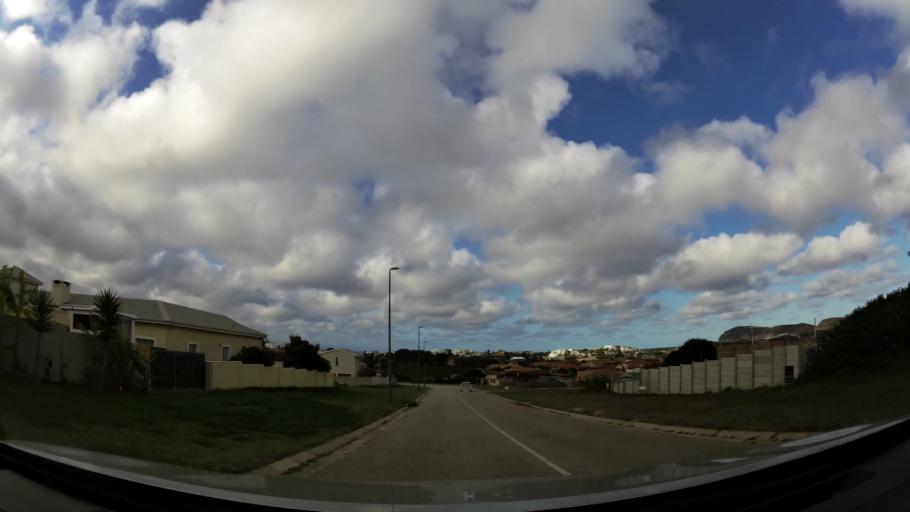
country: ZA
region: Western Cape
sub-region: Eden District Municipality
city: Plettenberg Bay
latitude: -34.0860
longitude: 23.3609
